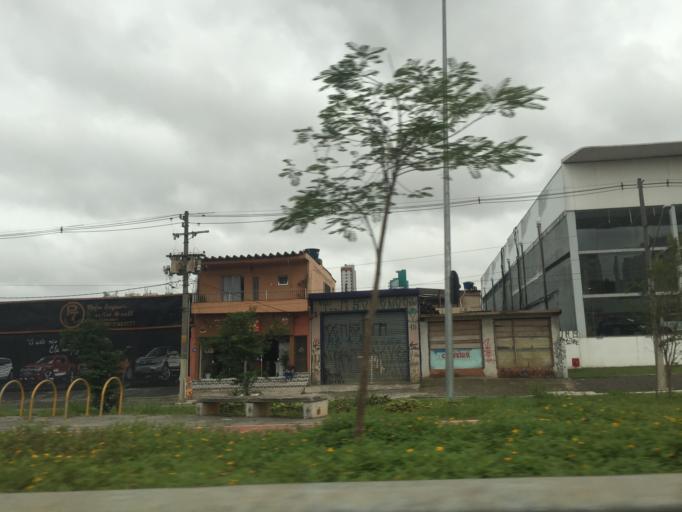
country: BR
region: Sao Paulo
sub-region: Sao Caetano Do Sul
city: Sao Caetano do Sul
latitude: -23.5838
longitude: -46.5757
